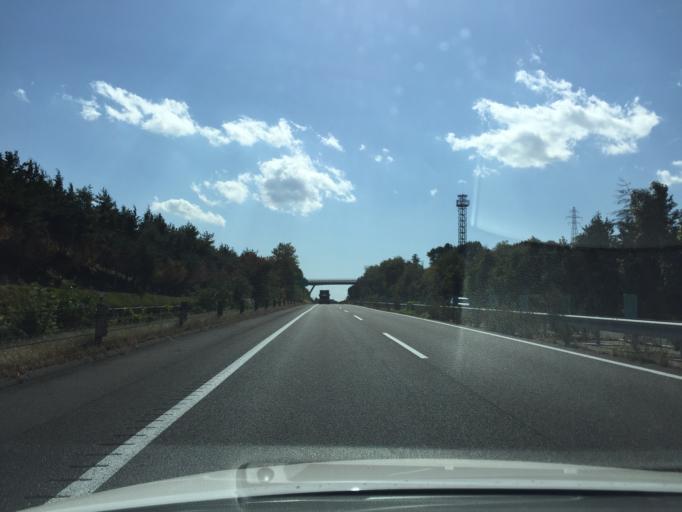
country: JP
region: Fukushima
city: Sukagawa
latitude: 37.2816
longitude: 140.3507
